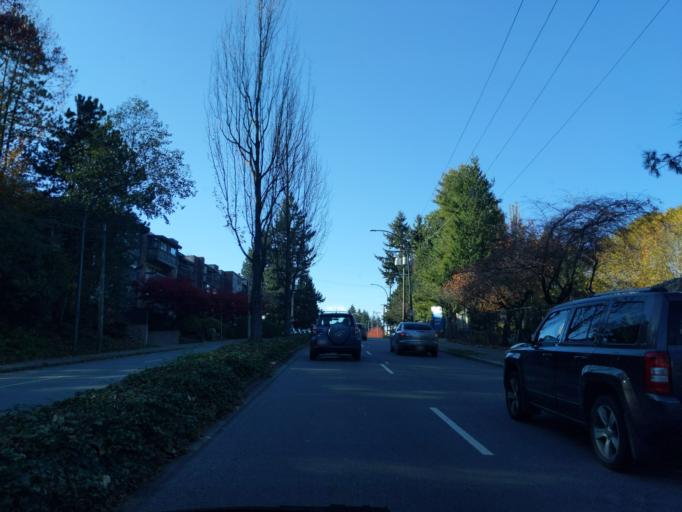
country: CA
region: British Columbia
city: New Westminster
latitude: 49.1864
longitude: -122.8524
